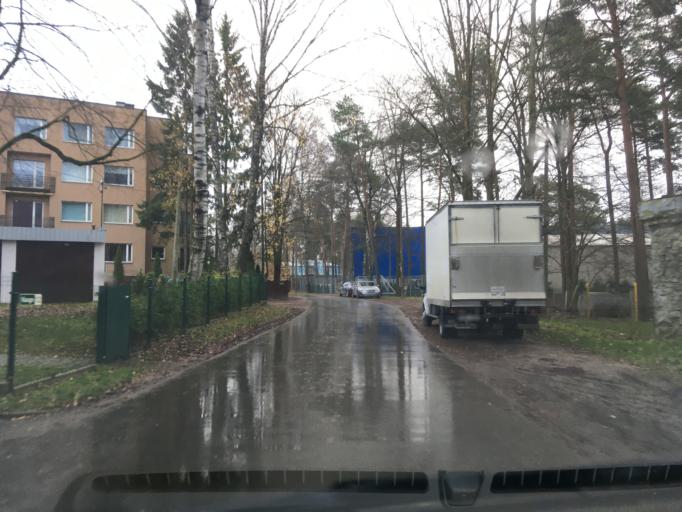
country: EE
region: Harju
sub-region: Tallinna linn
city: Tallinn
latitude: 59.3719
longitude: 24.7138
